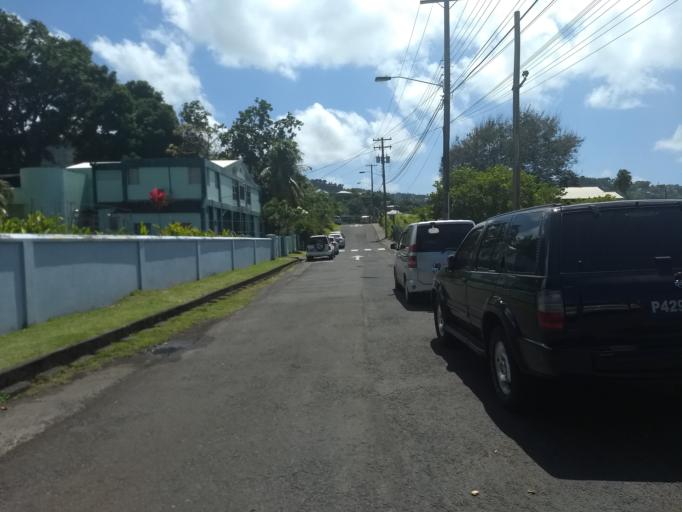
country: VC
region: Saint George
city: Kingstown
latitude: 13.1585
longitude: -61.2278
